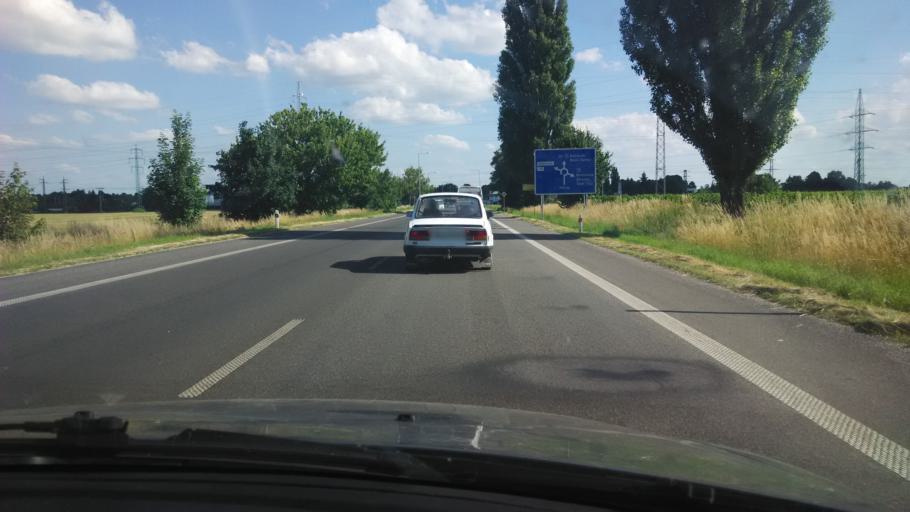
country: SK
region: Nitriansky
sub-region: Okres Nove Zamky
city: Nove Zamky
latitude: 48.0141
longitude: 18.1552
